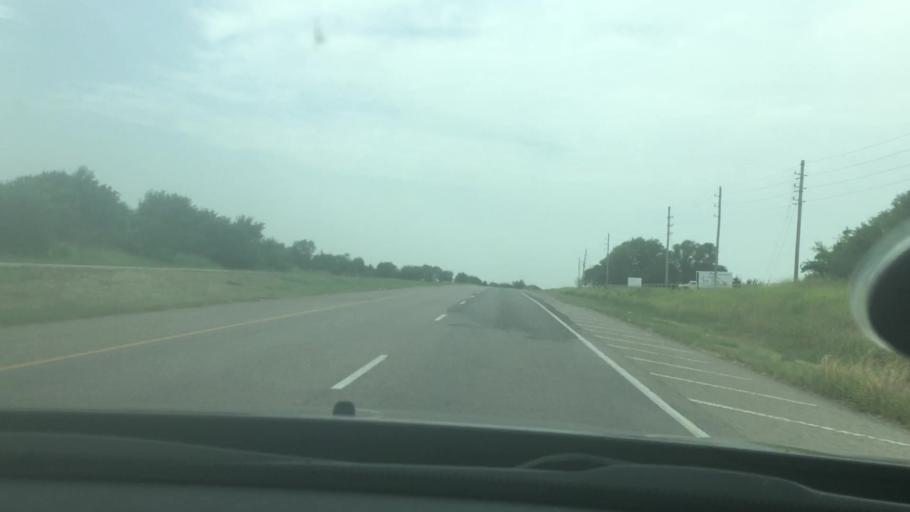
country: US
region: Oklahoma
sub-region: Pontotoc County
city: Ada
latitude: 34.7232
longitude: -96.7142
